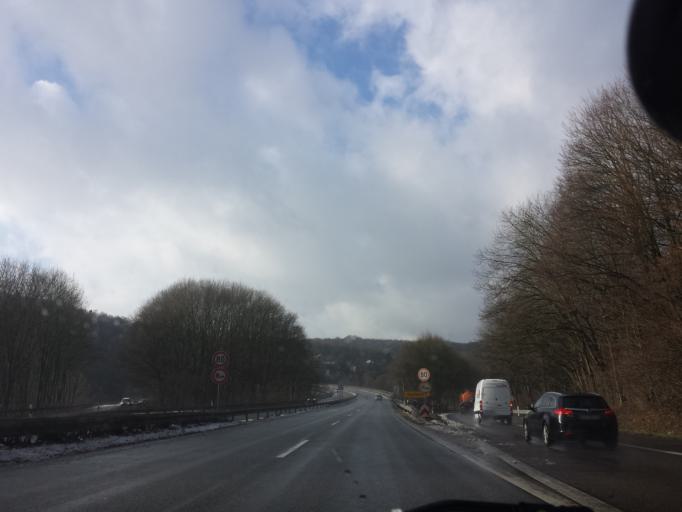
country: DE
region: North Rhine-Westphalia
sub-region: Regierungsbezirk Dusseldorf
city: Solingen
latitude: 51.2315
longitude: 7.1038
